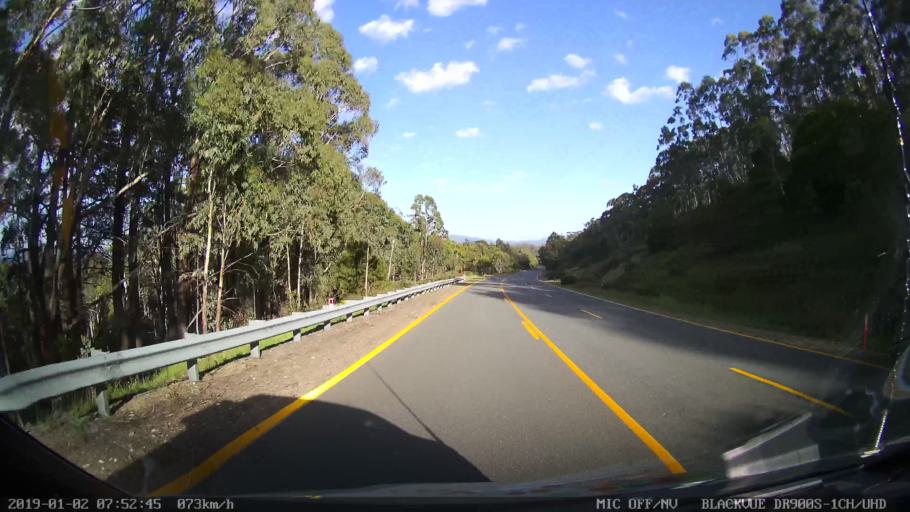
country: AU
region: New South Wales
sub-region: Tumut Shire
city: Tumut
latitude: -35.7126
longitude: 148.5144
